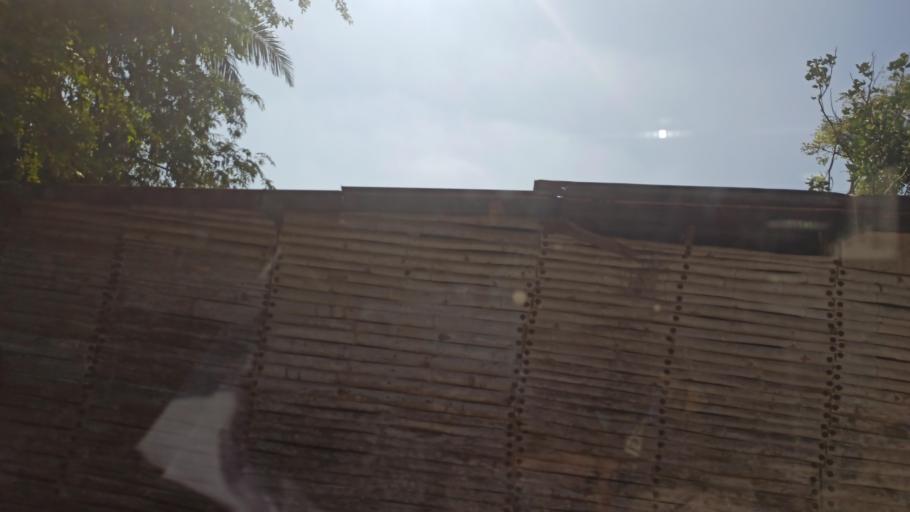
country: MX
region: Veracruz
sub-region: Martinez de la Torre
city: La Union Paso Largo
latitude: 20.1411
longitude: -97.0027
